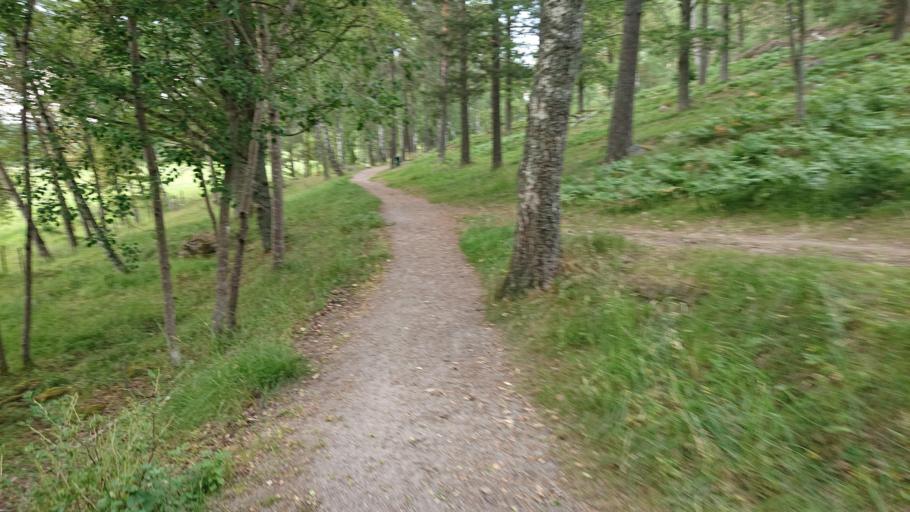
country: SE
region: Stockholm
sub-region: Osterakers Kommun
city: Akersberga
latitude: 59.4936
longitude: 18.2969
